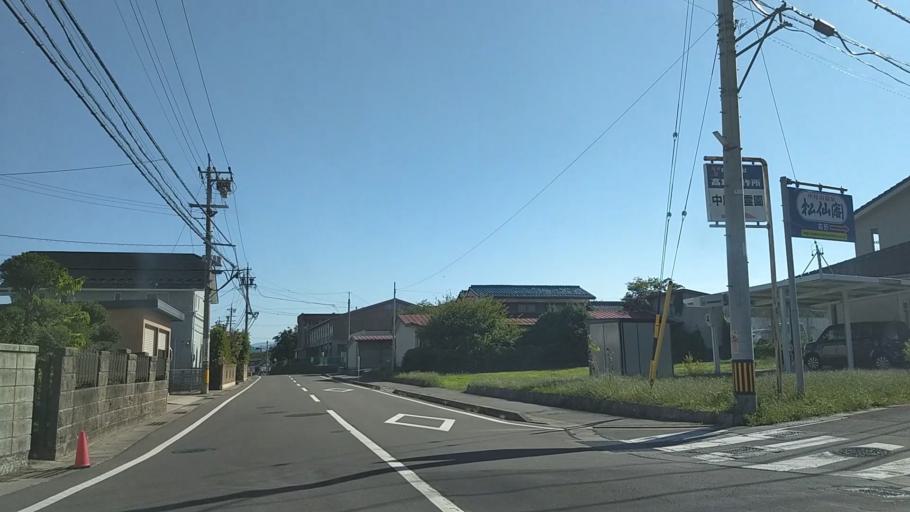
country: JP
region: Nagano
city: Nagano-shi
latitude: 36.6011
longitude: 138.1311
